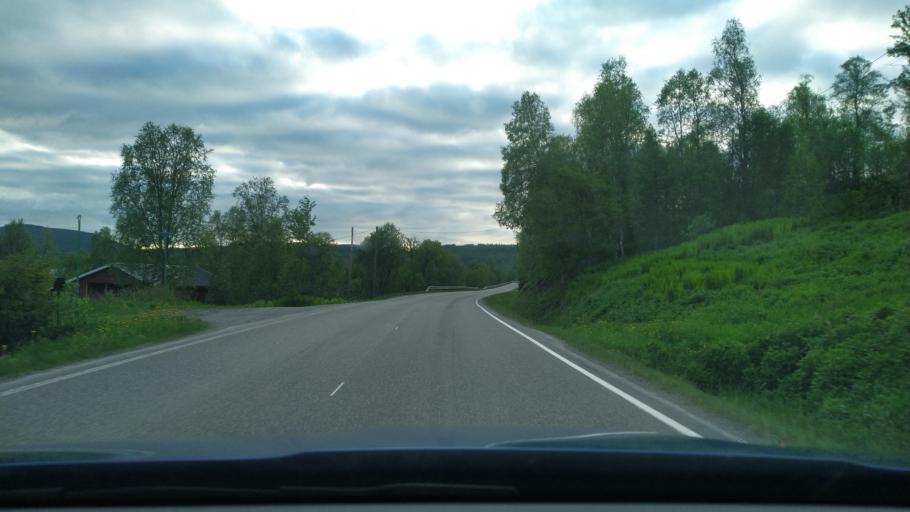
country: NO
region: Troms
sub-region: Sorreisa
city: Sorreisa
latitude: 69.0894
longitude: 18.3494
